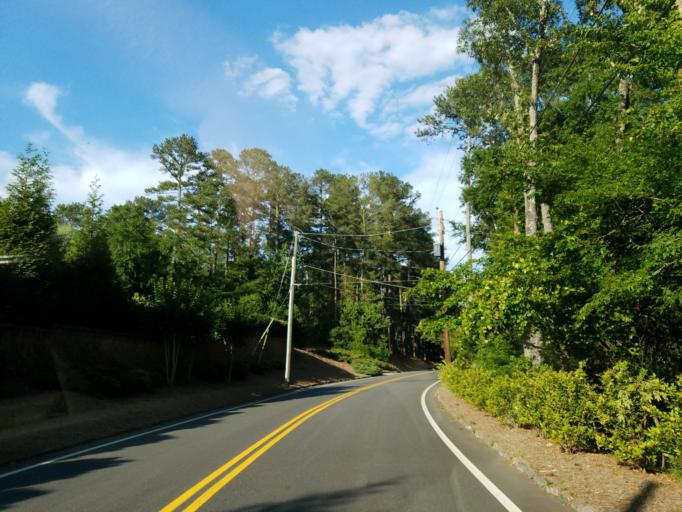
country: US
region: Georgia
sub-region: Cobb County
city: Vinings
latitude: 33.8808
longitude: -84.4308
